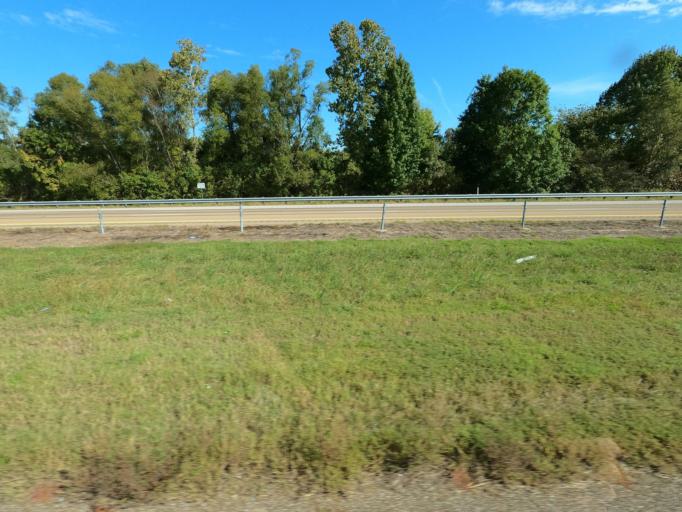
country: US
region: Tennessee
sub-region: Shelby County
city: Millington
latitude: 35.3122
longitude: -89.8611
